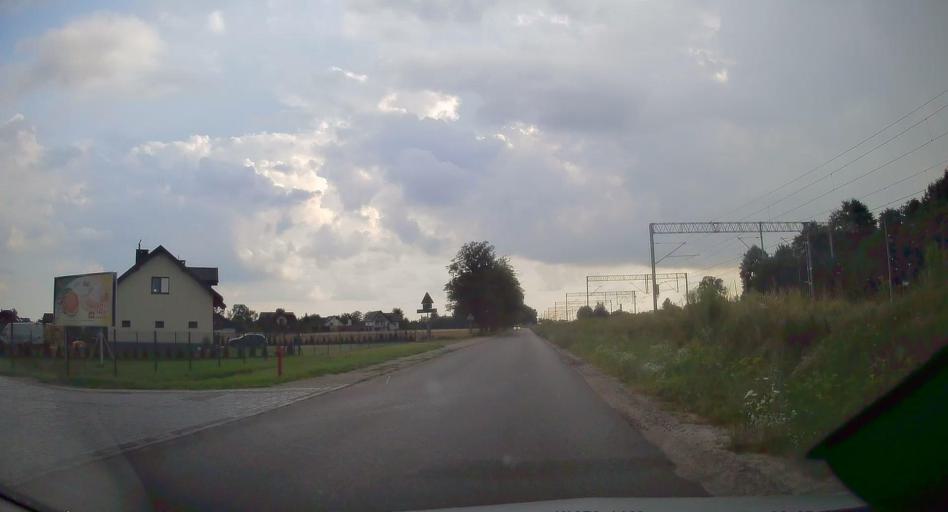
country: PL
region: Lodz Voivodeship
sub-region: Powiat brzezinski
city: Rogow
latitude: 51.8212
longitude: 19.8911
